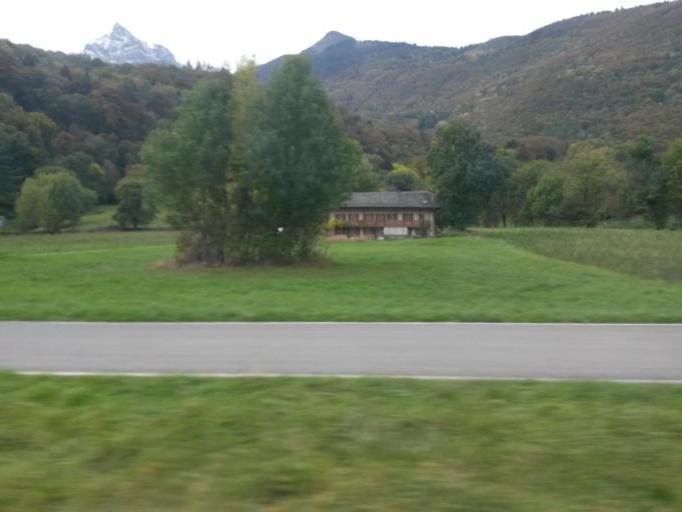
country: CH
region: Valais
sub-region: Saint-Maurice District
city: Saint-Maurice
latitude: 46.2332
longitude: 6.9964
